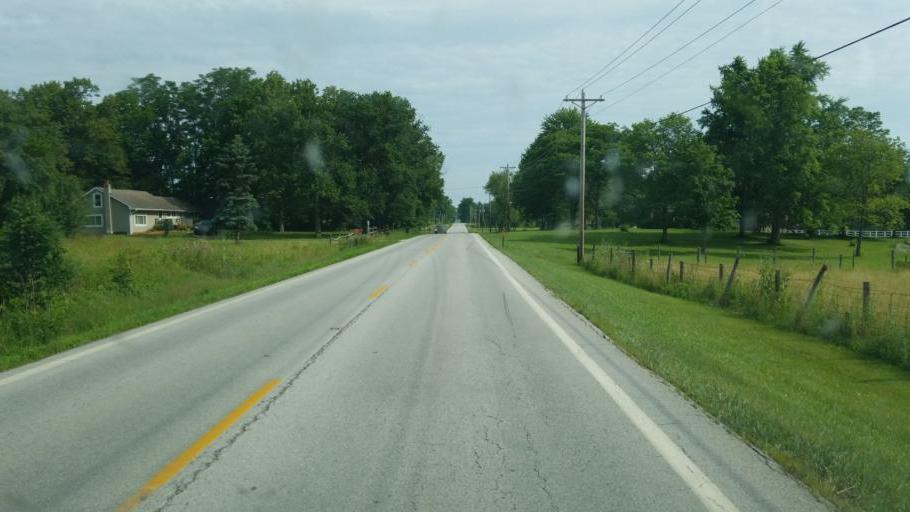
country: US
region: Ohio
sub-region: Medina County
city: Lodi
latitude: 41.0730
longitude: -82.0245
